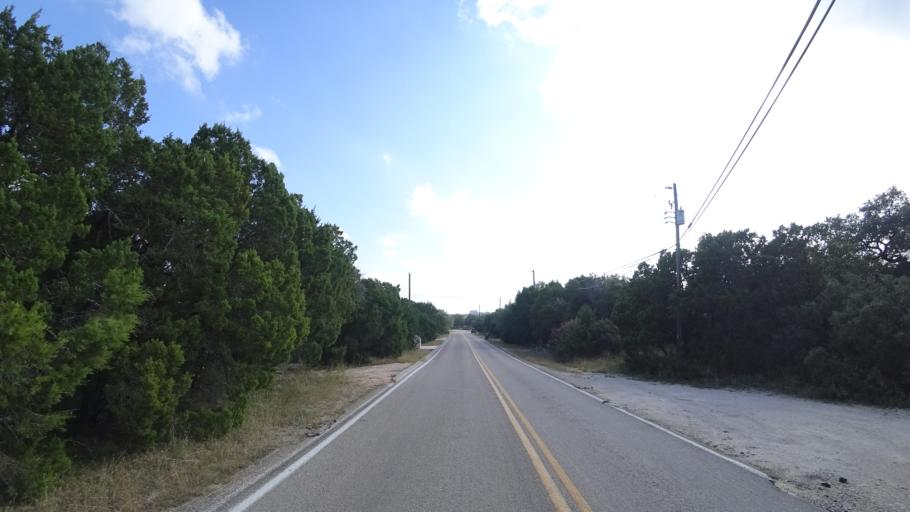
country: US
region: Texas
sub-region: Travis County
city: Barton Creek
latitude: 30.3083
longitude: -97.8661
